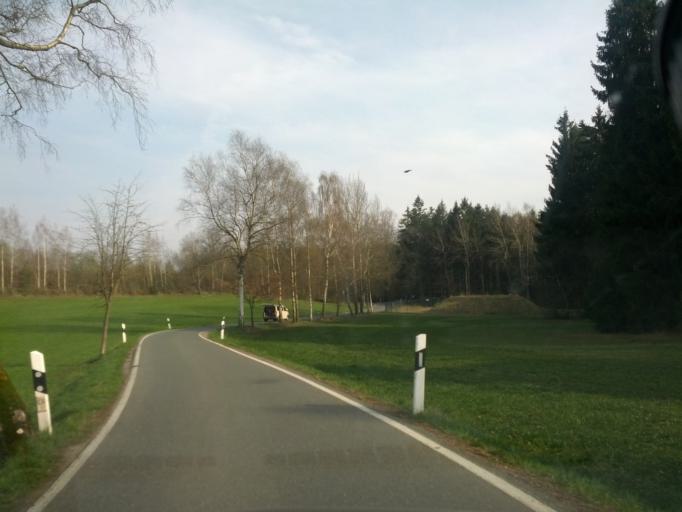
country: DE
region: Saxony
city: Kirchberg
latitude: 50.5793
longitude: 12.5182
